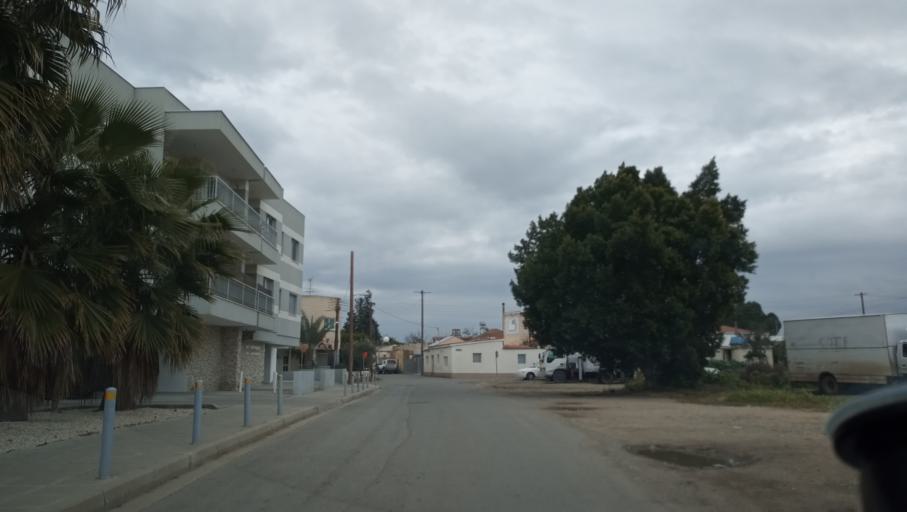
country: CY
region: Lefkosia
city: Pano Deftera
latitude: 35.0819
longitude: 33.2702
